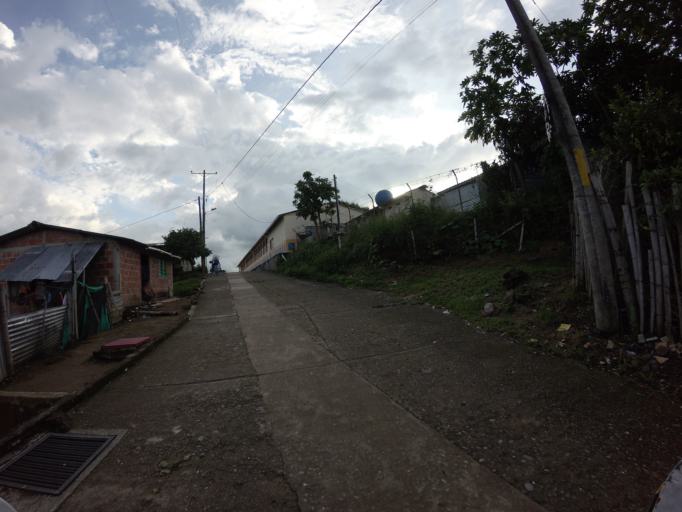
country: CO
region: Valle del Cauca
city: Ulloa
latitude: 4.7072
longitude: -75.7073
